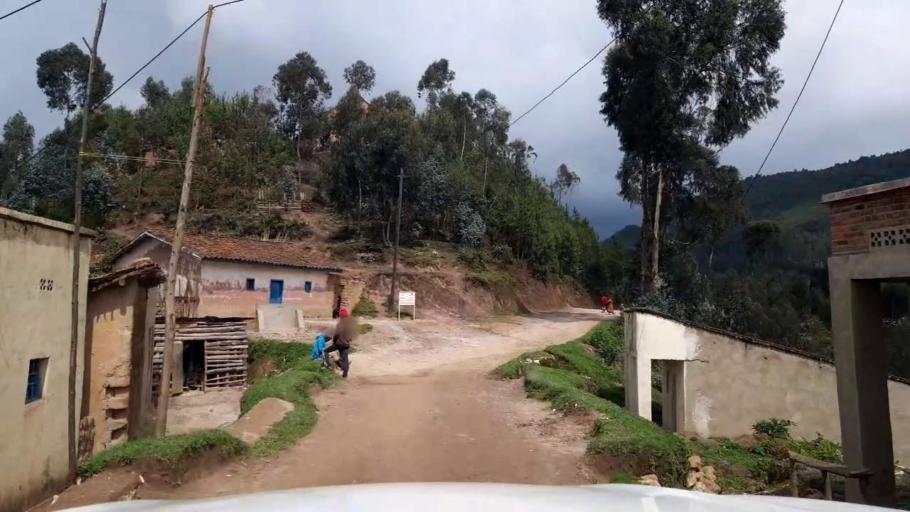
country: RW
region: Western Province
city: Kibuye
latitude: -1.9632
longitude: 29.4830
